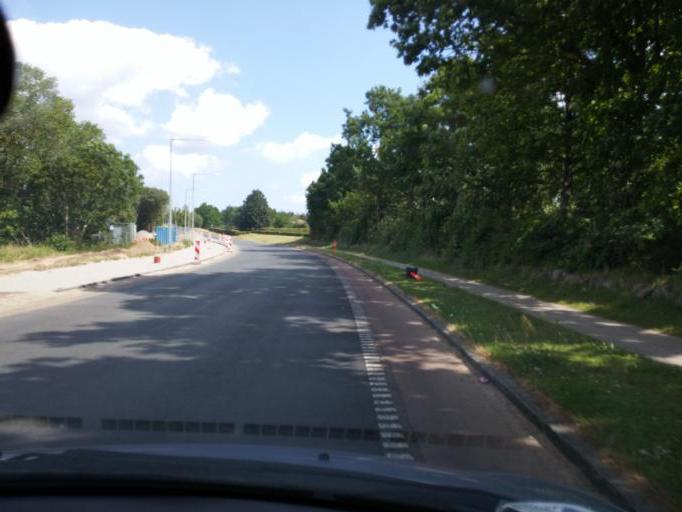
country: DK
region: South Denmark
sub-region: Kerteminde Kommune
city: Munkebo
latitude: 55.4571
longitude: 10.5522
